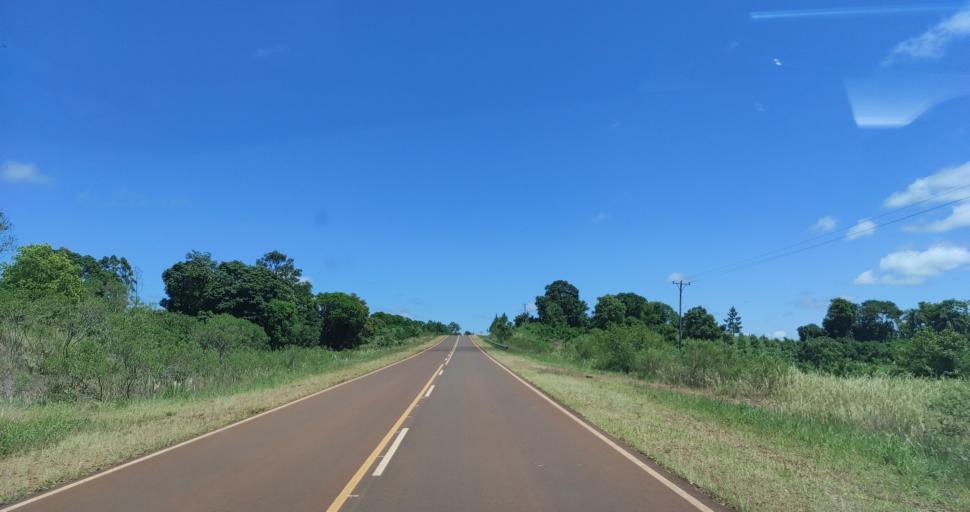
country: AR
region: Misiones
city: Campo Grande
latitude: -27.3241
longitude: -54.8936
